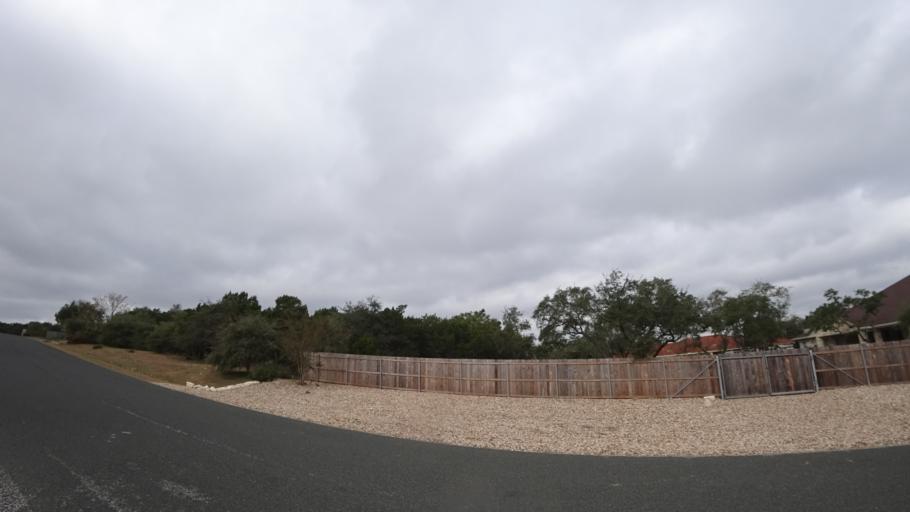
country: US
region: Texas
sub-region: Travis County
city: Barton Creek
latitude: 30.2519
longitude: -97.9097
